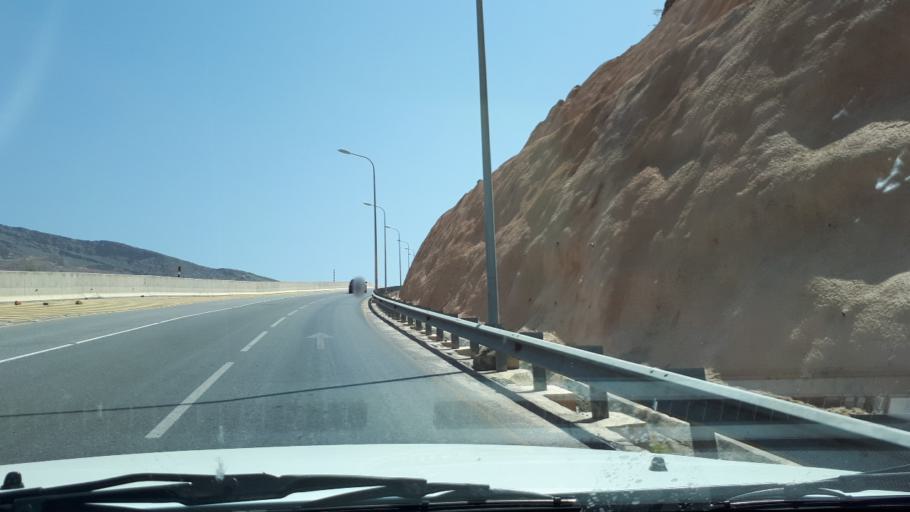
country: OM
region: Muhafazat ad Dakhiliyah
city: Izki
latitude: 22.9674
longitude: 57.6881
